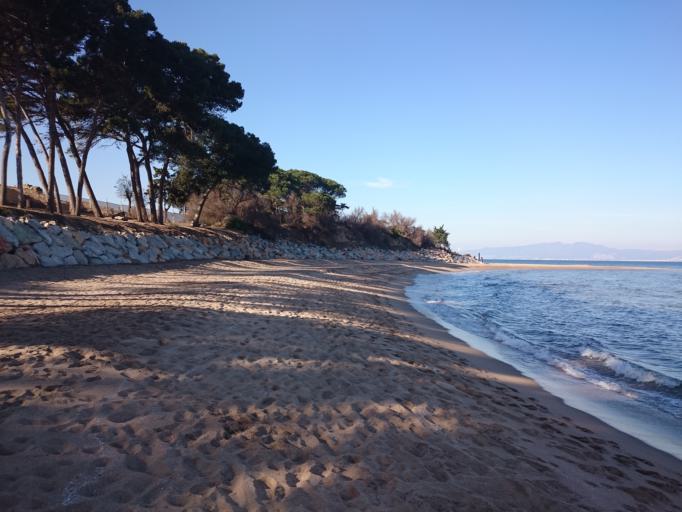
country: ES
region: Catalonia
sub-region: Provincia de Girona
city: l'Escala
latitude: 42.1339
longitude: 3.1218
